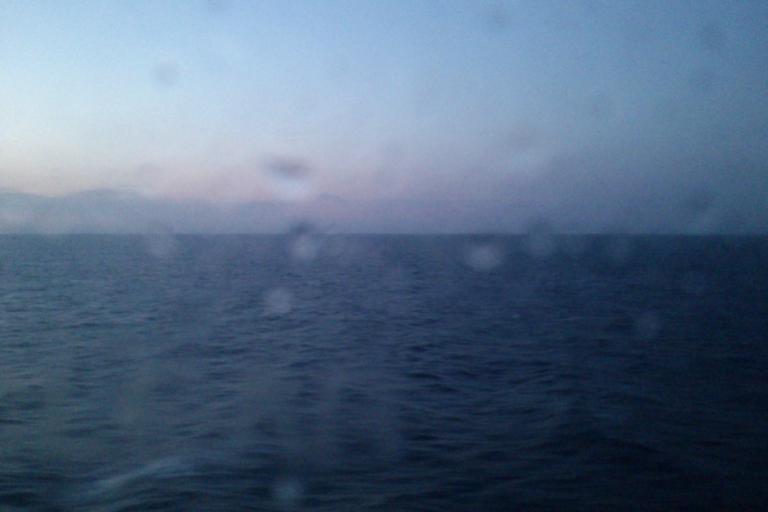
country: JP
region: Ishikawa
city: Kanazawa-shi
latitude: 37.0584
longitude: 136.0030
